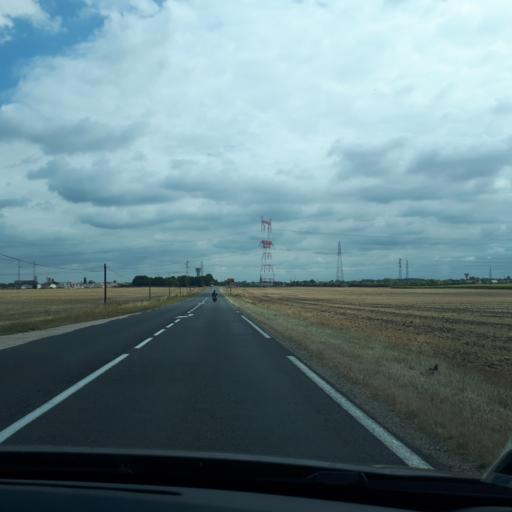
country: FR
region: Centre
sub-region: Departement du Loiret
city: Ormes
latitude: 47.9402
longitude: 1.7974
